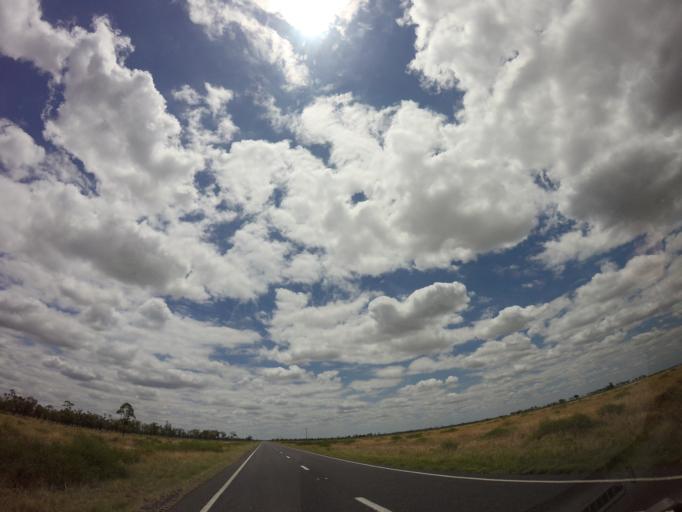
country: AU
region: New South Wales
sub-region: Moree Plains
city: Boggabilla
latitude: -28.6739
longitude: 150.3128
